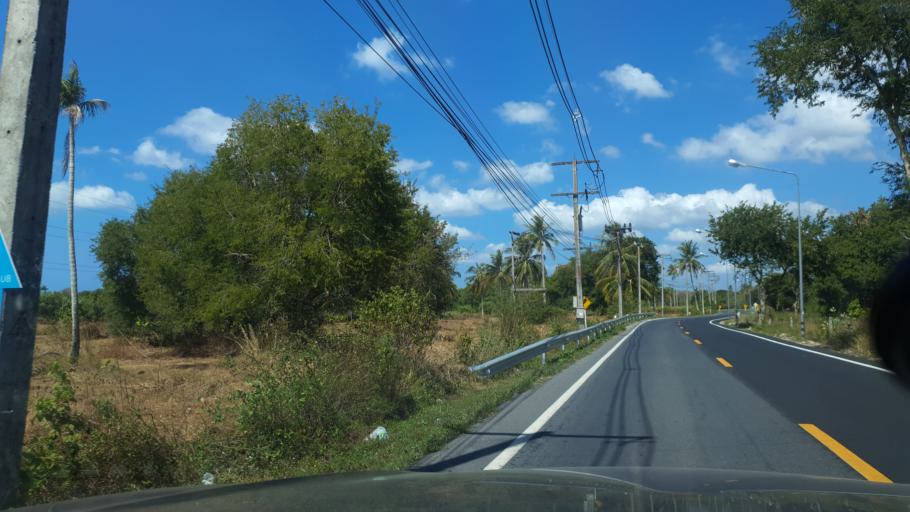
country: TH
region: Phuket
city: Thalang
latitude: 8.1530
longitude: 98.3052
